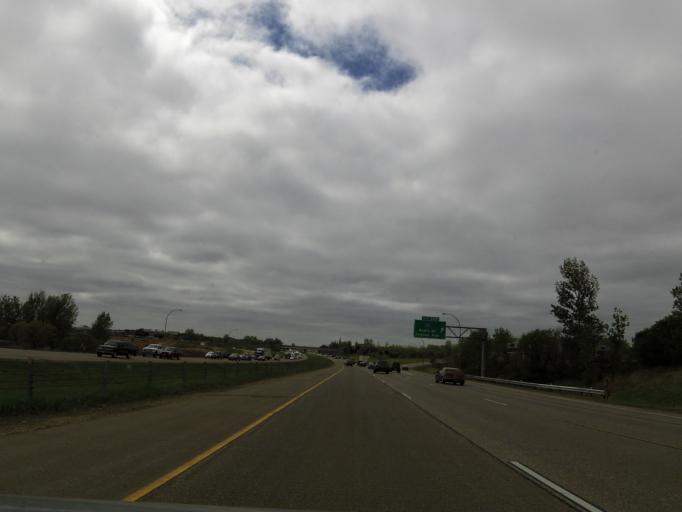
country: US
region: Minnesota
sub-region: Washington County
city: Oakdale
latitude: 44.9489
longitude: -92.9254
